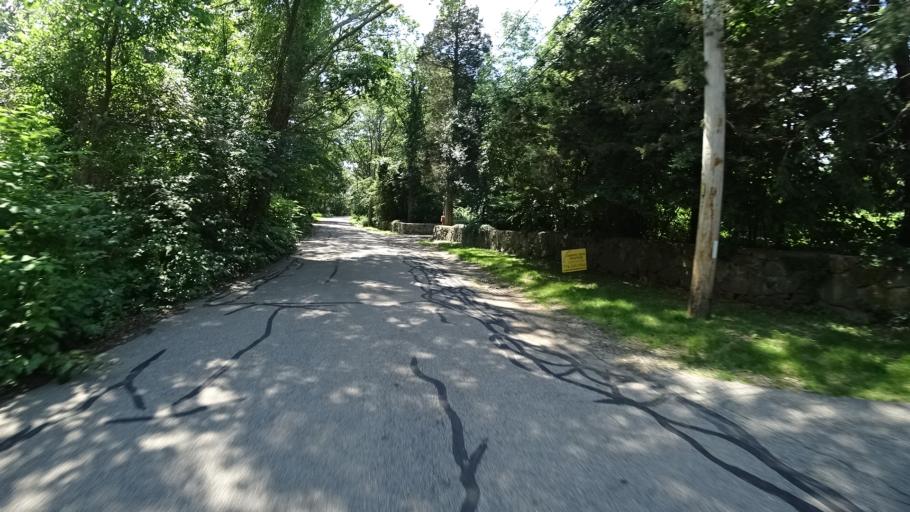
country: US
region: Massachusetts
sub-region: Norfolk County
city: Dedham
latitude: 42.2513
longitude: -71.2050
